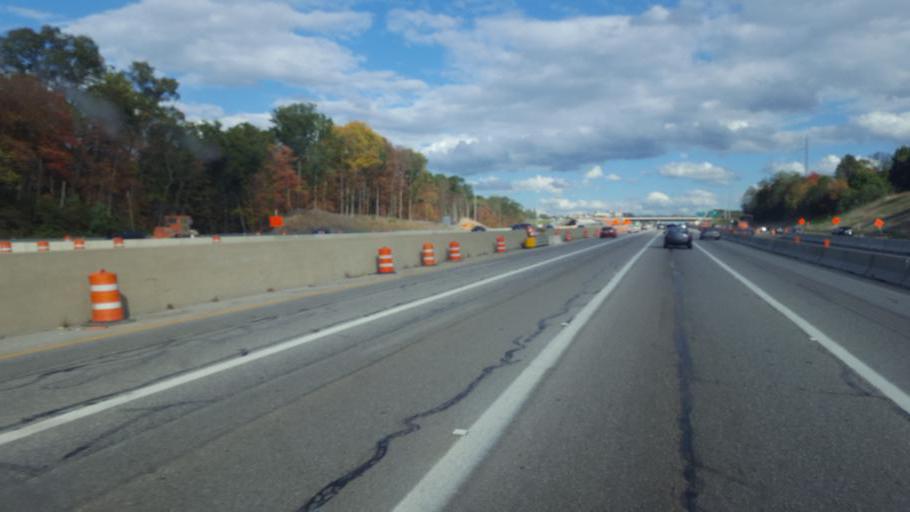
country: US
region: Ohio
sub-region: Franklin County
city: Worthington
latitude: 40.1120
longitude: -83.0273
